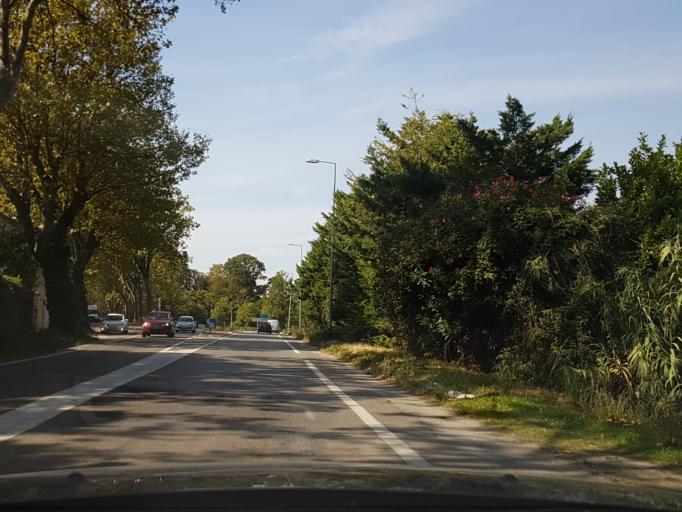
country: FR
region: Provence-Alpes-Cote d'Azur
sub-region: Departement des Bouches-du-Rhone
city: Saint-Remy-de-Provence
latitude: 43.7868
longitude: 4.8541
